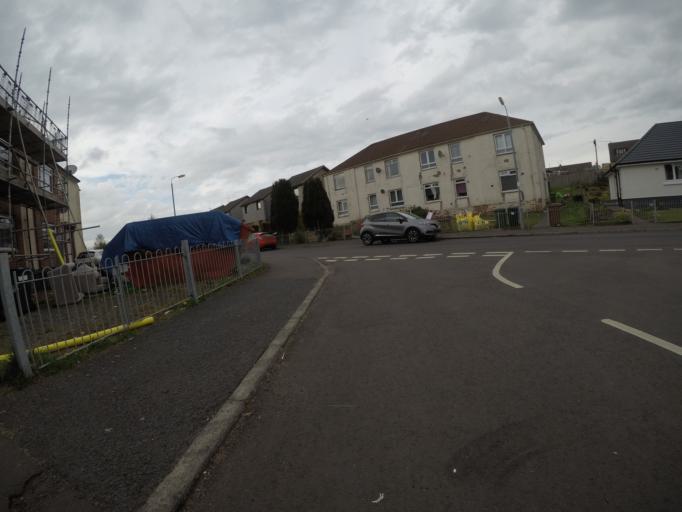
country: GB
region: Scotland
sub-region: East Ayrshire
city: Kilmaurs
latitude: 55.6413
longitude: -4.5294
